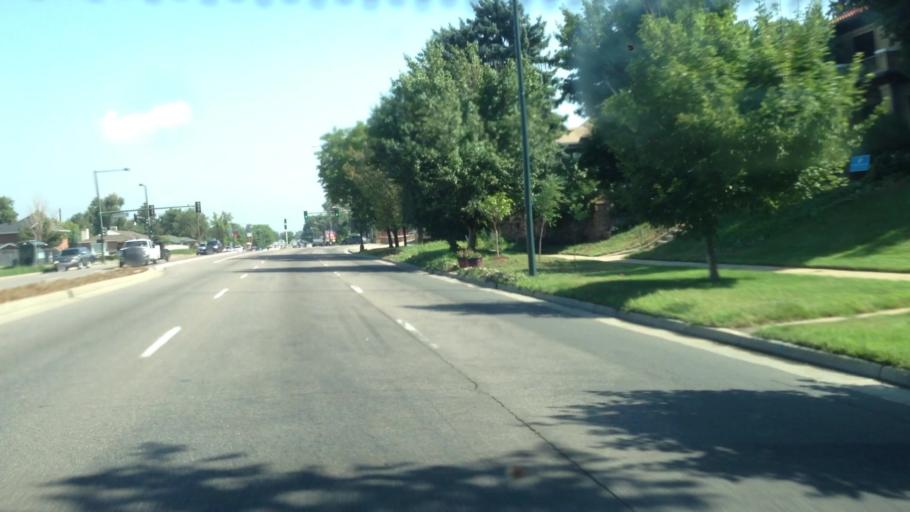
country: US
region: Colorado
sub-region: Denver County
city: Denver
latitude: 39.7533
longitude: -104.9407
